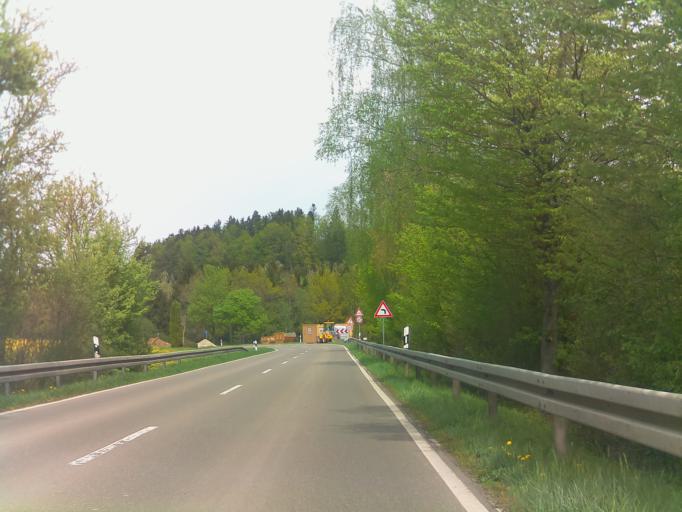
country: DE
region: Baden-Wuerttemberg
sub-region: Freiburg Region
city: Deisslingen
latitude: 48.1336
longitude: 8.6292
